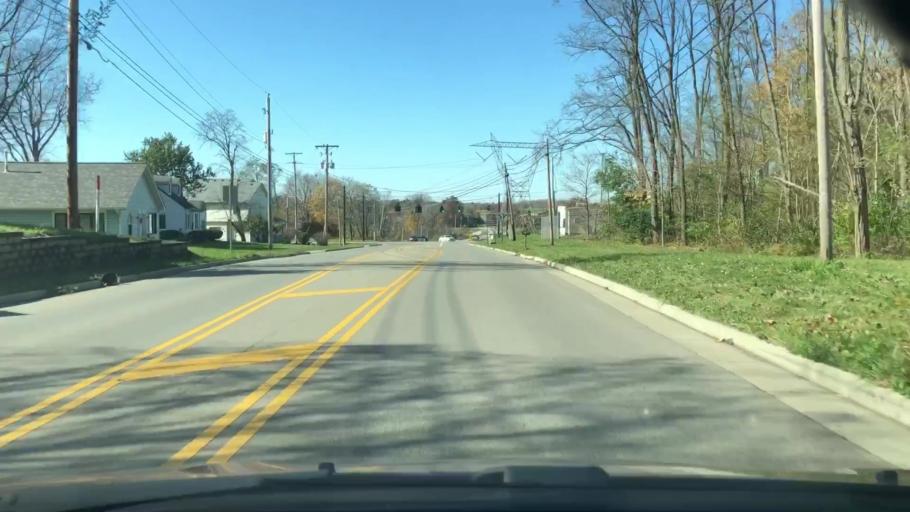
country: US
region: Ohio
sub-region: Delaware County
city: Lewis Center
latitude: 40.1822
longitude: -82.9549
